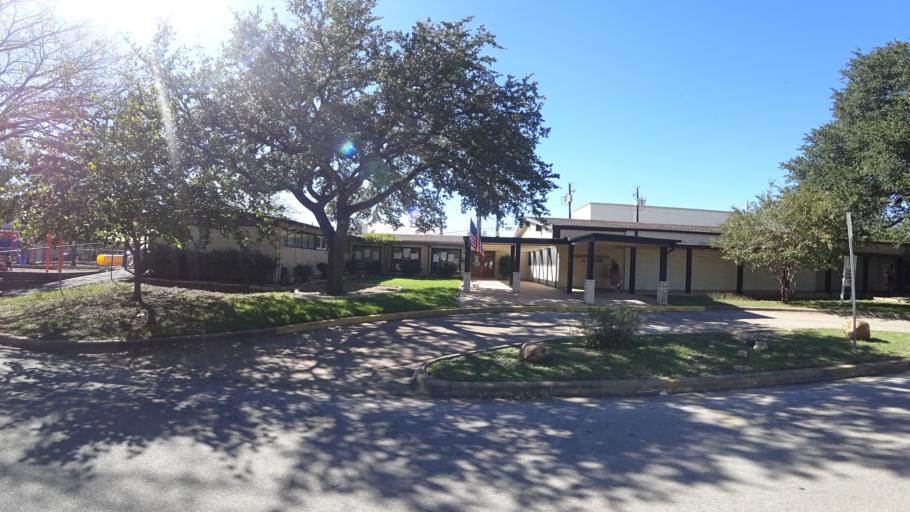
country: US
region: Texas
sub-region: Travis County
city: Austin
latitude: 30.3336
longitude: -97.7388
